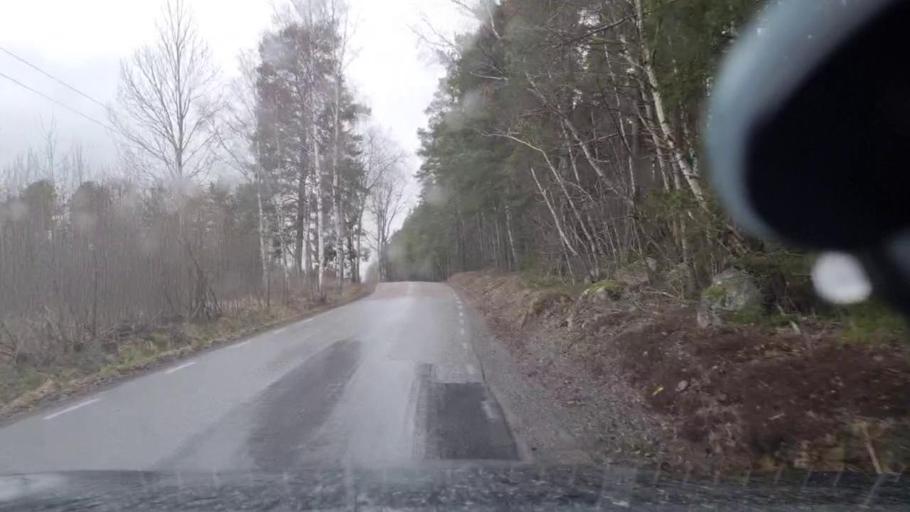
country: SE
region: Stockholm
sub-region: Taby Kommun
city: Taby
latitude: 59.4860
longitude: 18.0125
